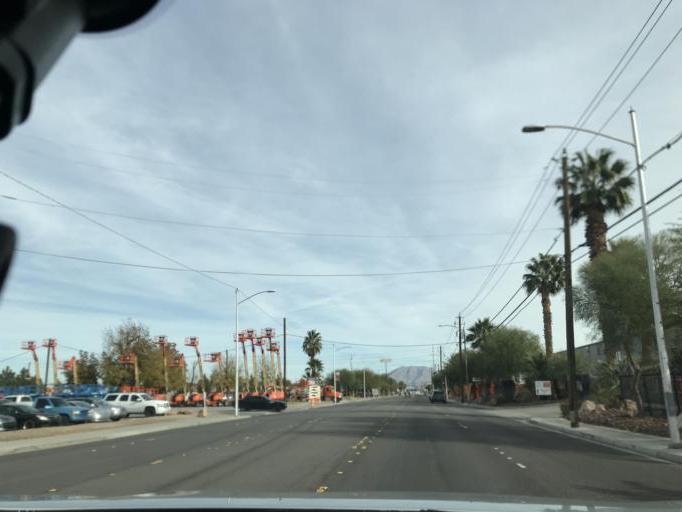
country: US
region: Nevada
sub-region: Clark County
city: Las Vegas
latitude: 36.1771
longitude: -115.1662
